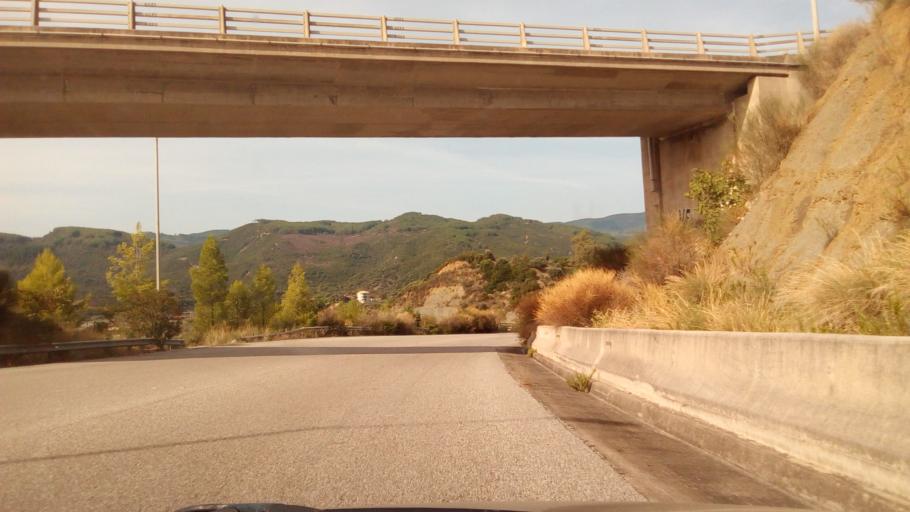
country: GR
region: West Greece
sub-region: Nomos Aitolias kai Akarnanias
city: Nafpaktos
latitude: 38.3999
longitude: 21.8017
